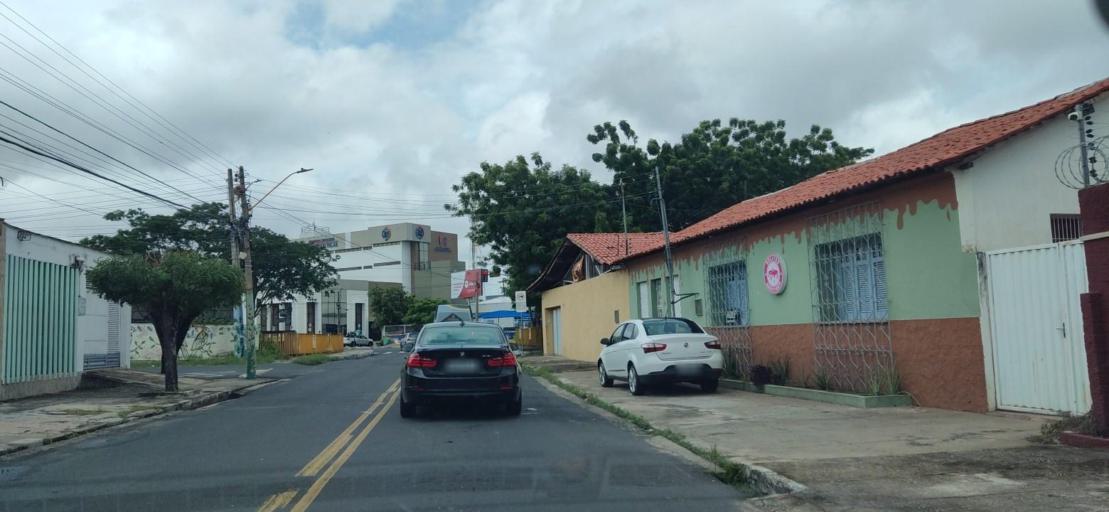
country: BR
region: Piaui
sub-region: Teresina
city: Teresina
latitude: -5.0809
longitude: -42.8075
